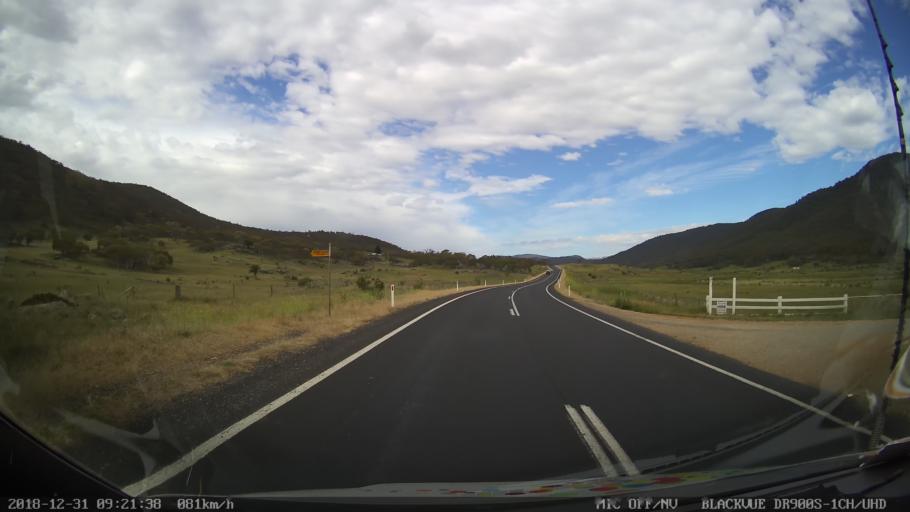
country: AU
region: New South Wales
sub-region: Snowy River
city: Jindabyne
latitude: -36.4303
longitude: 148.5585
